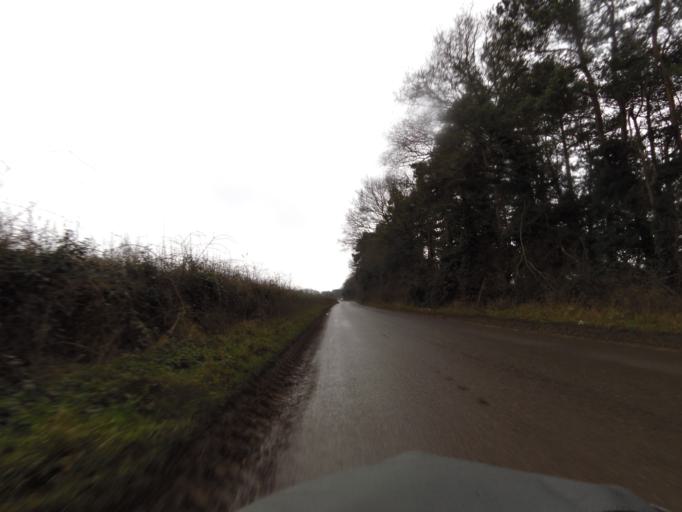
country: GB
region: England
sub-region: Norfolk
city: Briston
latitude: 52.8904
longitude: 1.0849
